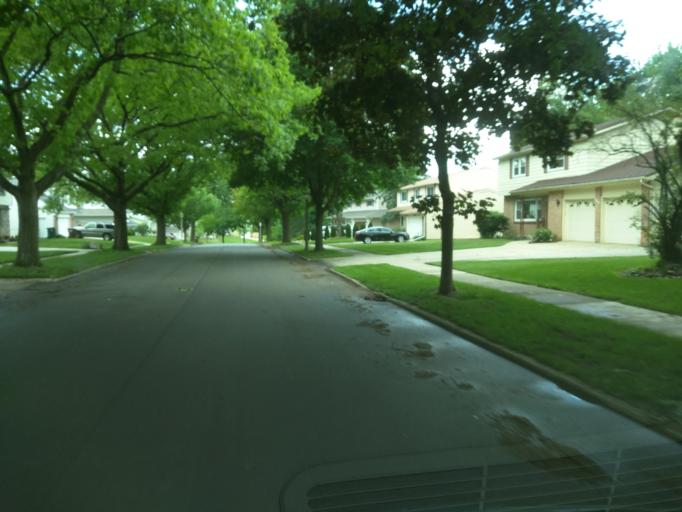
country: US
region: Michigan
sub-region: Eaton County
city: Waverly
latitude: 42.7048
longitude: -84.5978
